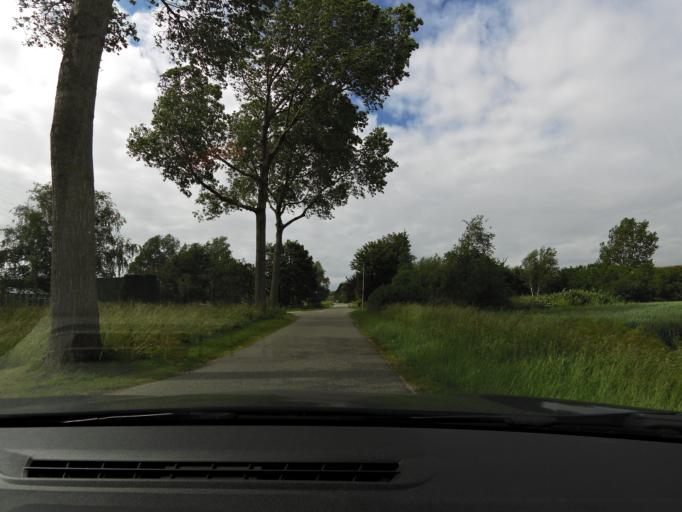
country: NL
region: South Holland
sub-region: Gemeente Brielle
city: Brielle
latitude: 51.9178
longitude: 4.1267
